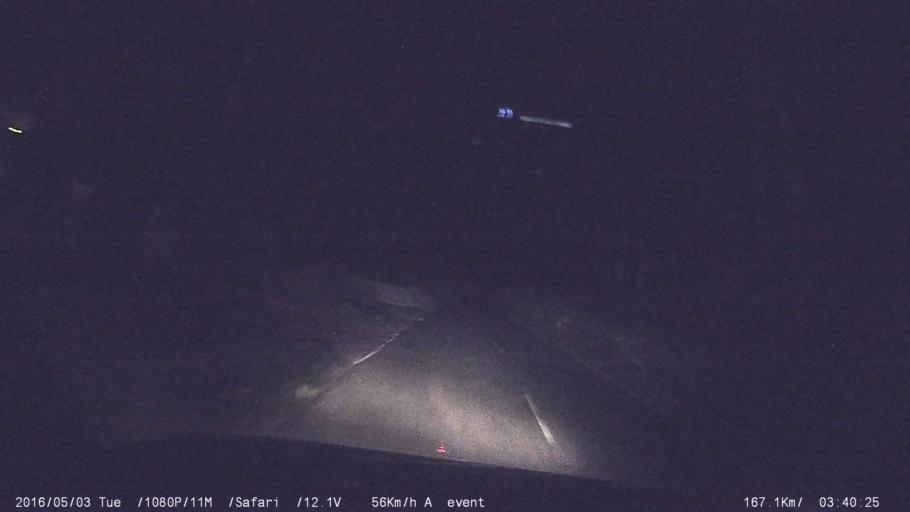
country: IN
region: Kerala
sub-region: Kottayam
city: Palackattumala
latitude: 9.7609
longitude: 76.6094
